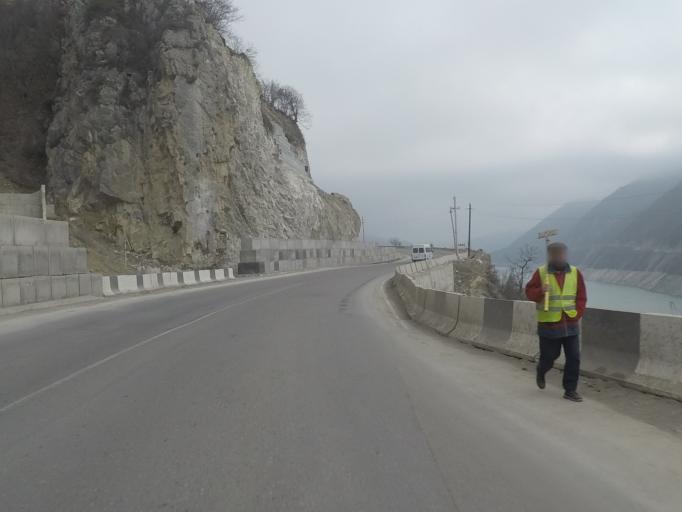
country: GE
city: Zhinvali
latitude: 42.1407
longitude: 44.7682
